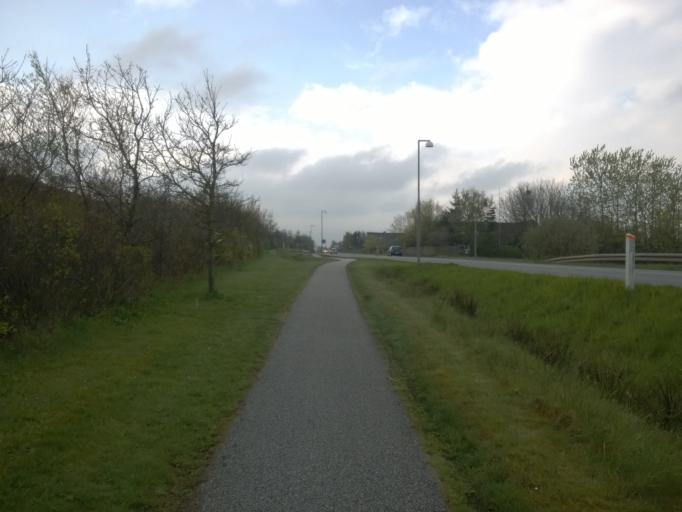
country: DK
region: Central Jutland
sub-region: Holstebro Kommune
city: Vinderup
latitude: 56.4740
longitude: 8.7750
